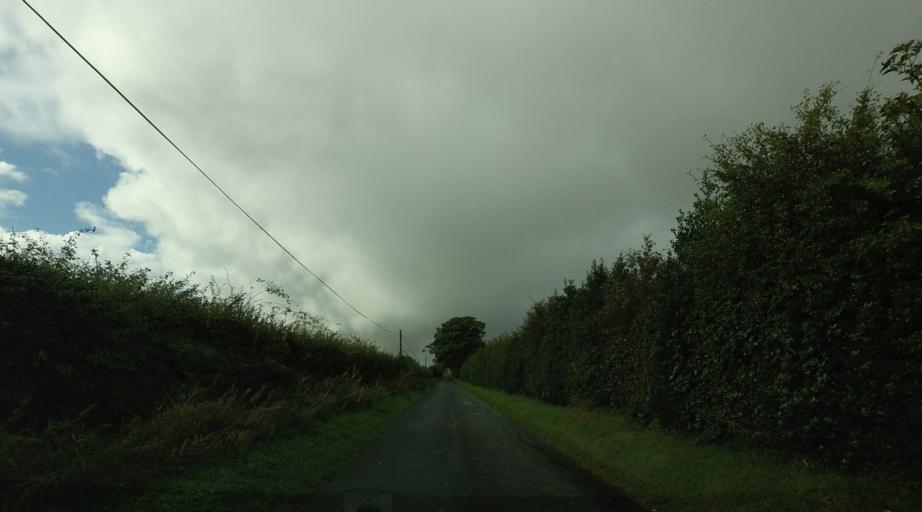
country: GB
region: Scotland
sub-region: Fife
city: Balmullo
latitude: 56.3603
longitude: -2.9458
